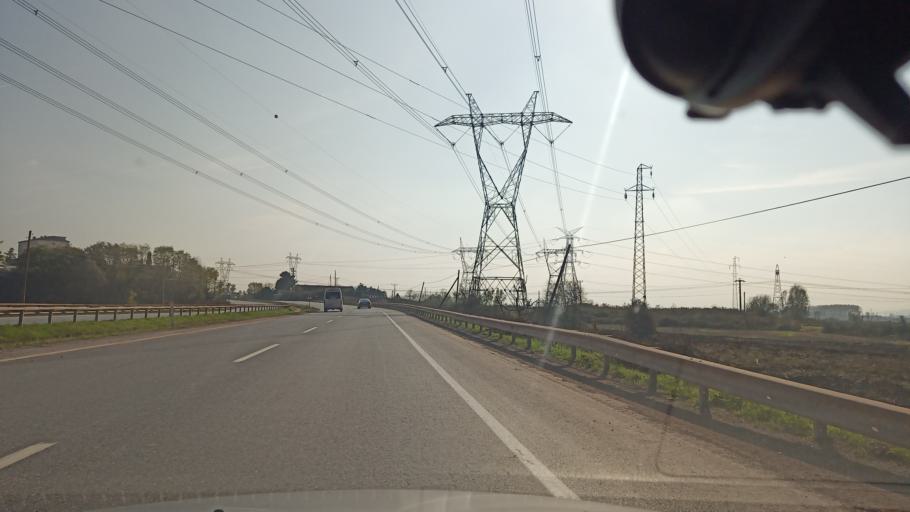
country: TR
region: Sakarya
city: Adapazari
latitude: 40.8253
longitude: 30.3916
